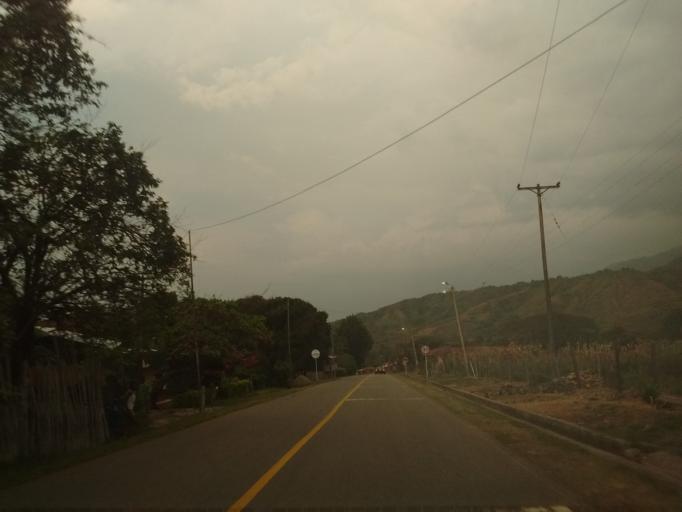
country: CO
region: Cauca
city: Caloto
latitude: 3.0712
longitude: -76.3535
